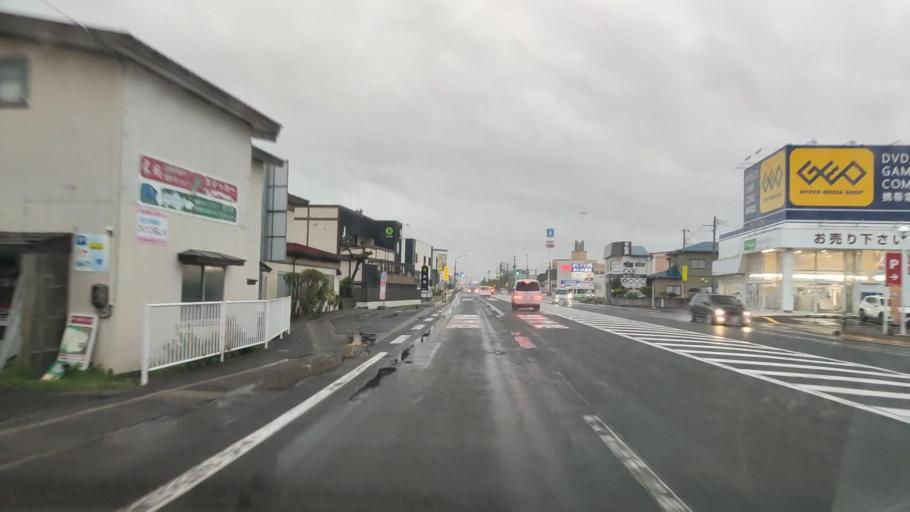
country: JP
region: Akita
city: Akita
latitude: 39.6948
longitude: 140.1201
